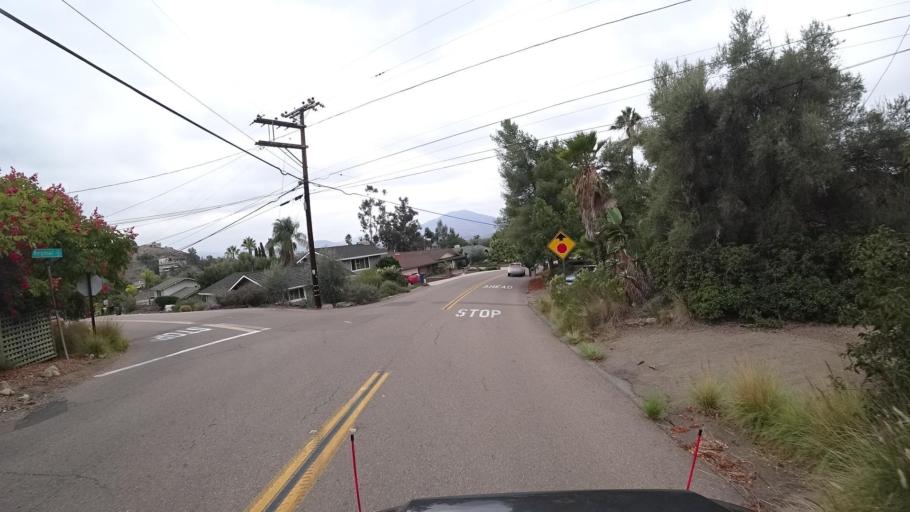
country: US
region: California
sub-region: San Diego County
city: Casa de Oro-Mount Helix
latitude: 32.7589
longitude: -116.9774
